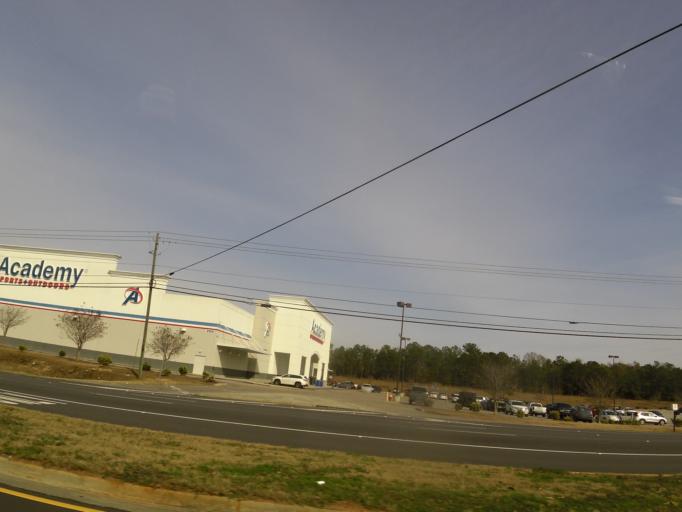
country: US
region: Alabama
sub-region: Houston County
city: Dothan
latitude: 31.2602
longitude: -85.4367
